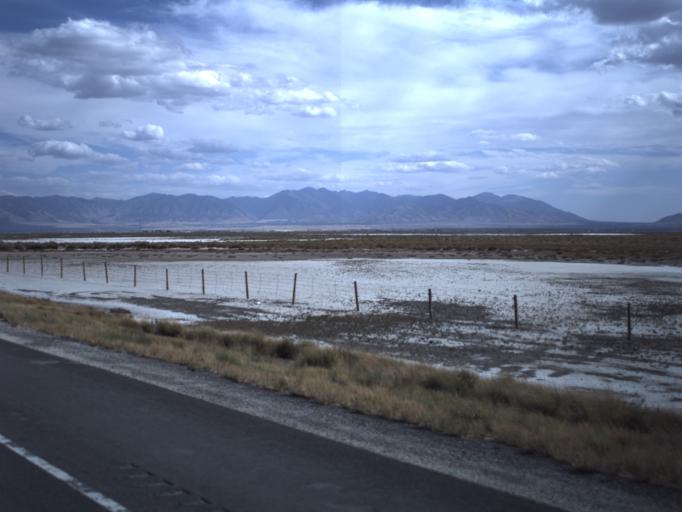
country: US
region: Utah
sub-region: Tooele County
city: Grantsville
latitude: 40.7027
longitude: -112.5013
